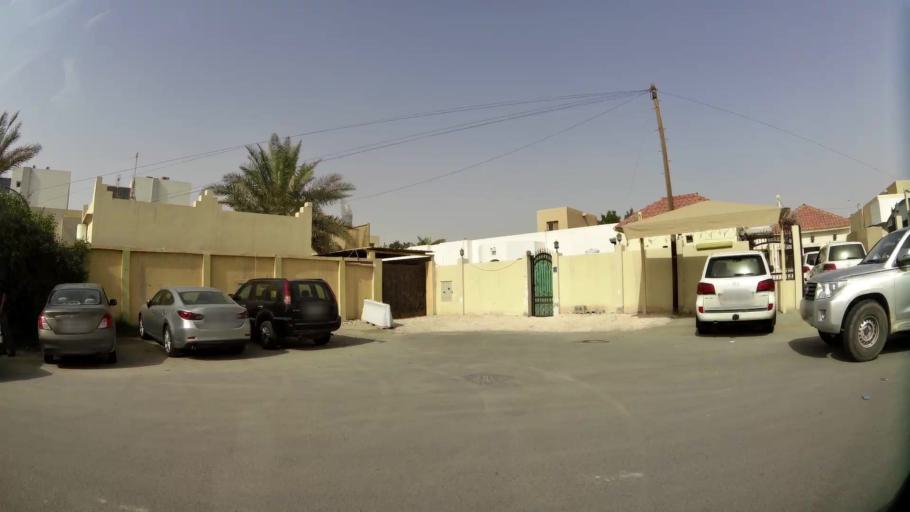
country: QA
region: Baladiyat ar Rayyan
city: Ar Rayyan
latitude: 25.2511
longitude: 51.4398
